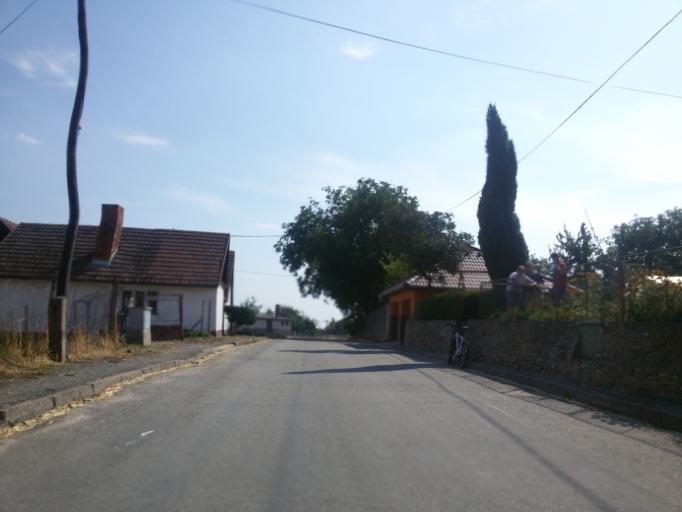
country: CZ
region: South Moravian
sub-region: Okres Brno-Venkov
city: Lomnice
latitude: 49.4429
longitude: 16.4566
